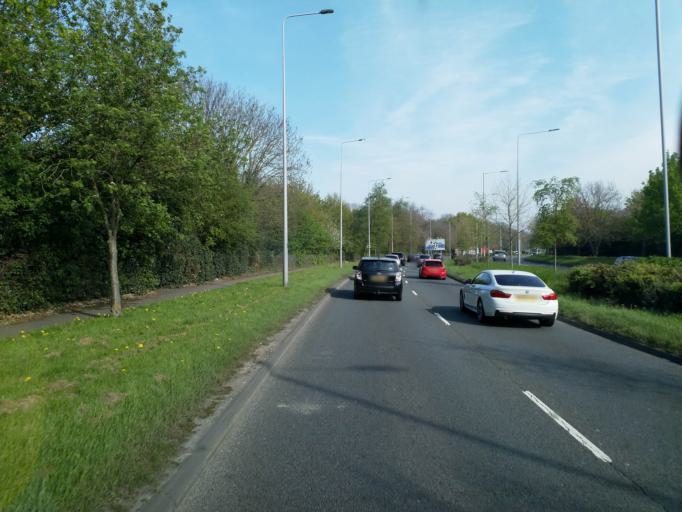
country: GB
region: England
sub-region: Greater London
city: Hayes
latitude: 51.4867
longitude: -0.4112
